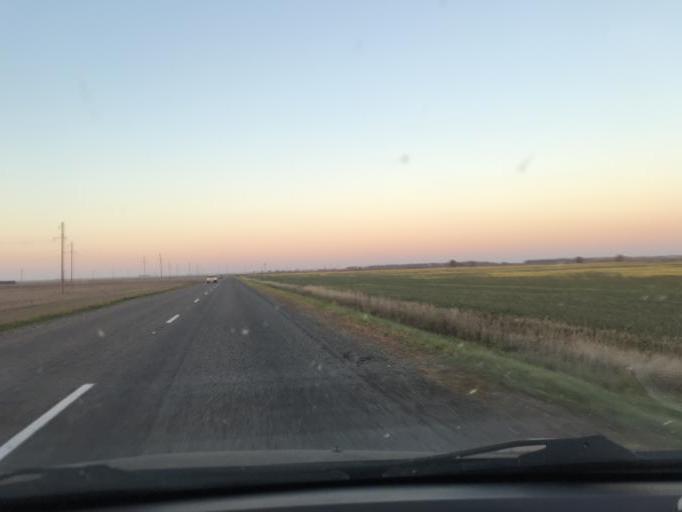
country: BY
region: Gomel
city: Loyew
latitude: 52.1273
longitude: 30.5855
